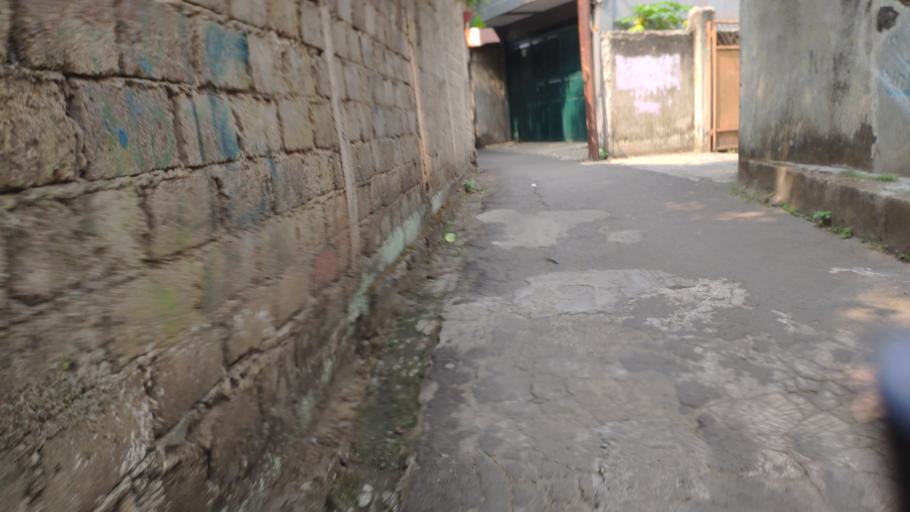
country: ID
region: West Java
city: Pamulang
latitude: -6.3123
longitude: 106.8103
